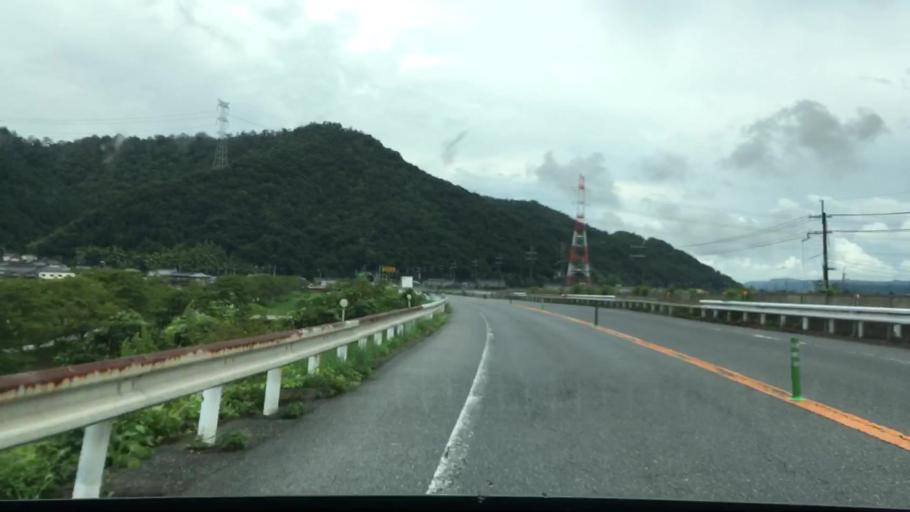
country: JP
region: Hyogo
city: Himeji
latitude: 34.9768
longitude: 134.7687
